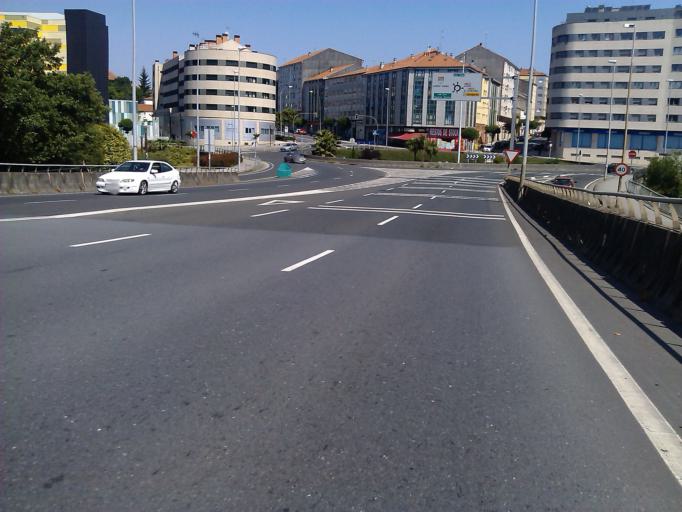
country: ES
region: Galicia
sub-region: Provincia da Coruna
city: Santiago de Compostela
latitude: 42.8665
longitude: -8.5442
